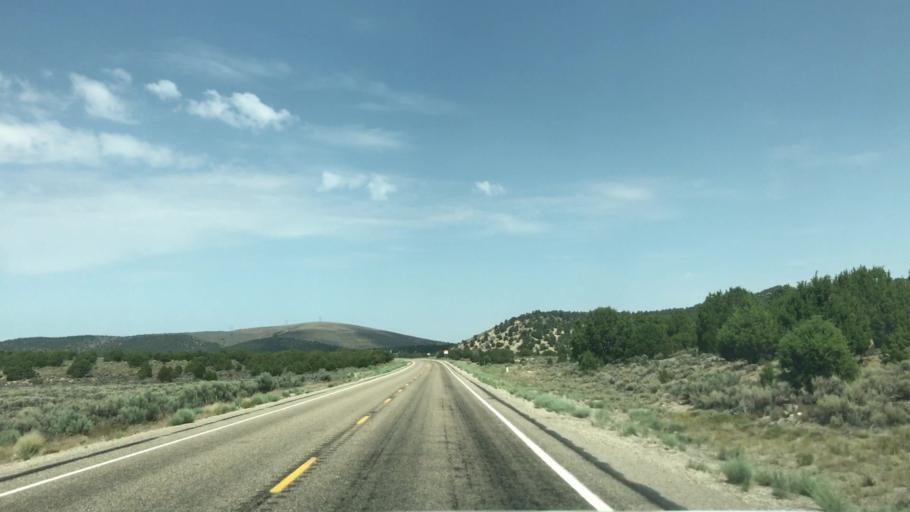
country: US
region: Nevada
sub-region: White Pine County
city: Ely
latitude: 39.3782
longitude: -115.0640
